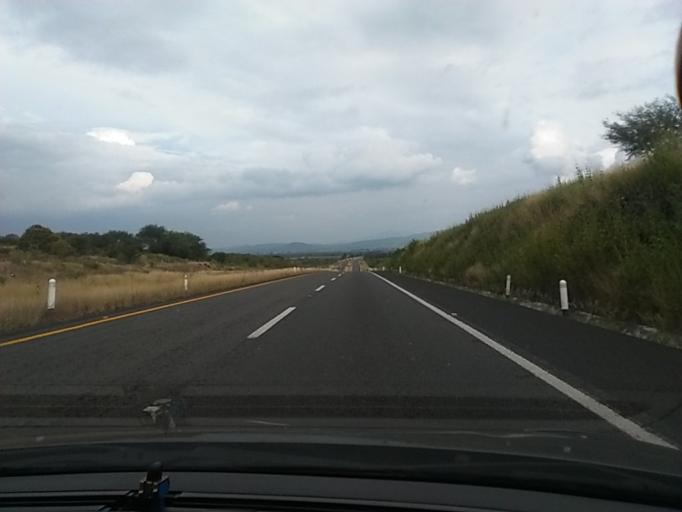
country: MX
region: Michoacan
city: Ixtlan
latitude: 20.1846
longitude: -102.2977
